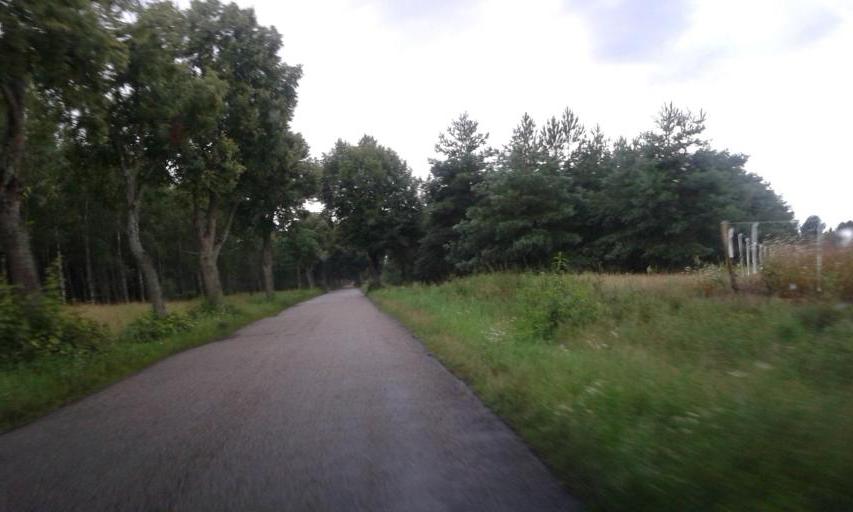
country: PL
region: Greater Poland Voivodeship
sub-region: Powiat zlotowski
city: Sypniewo
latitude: 53.4671
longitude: 16.5058
